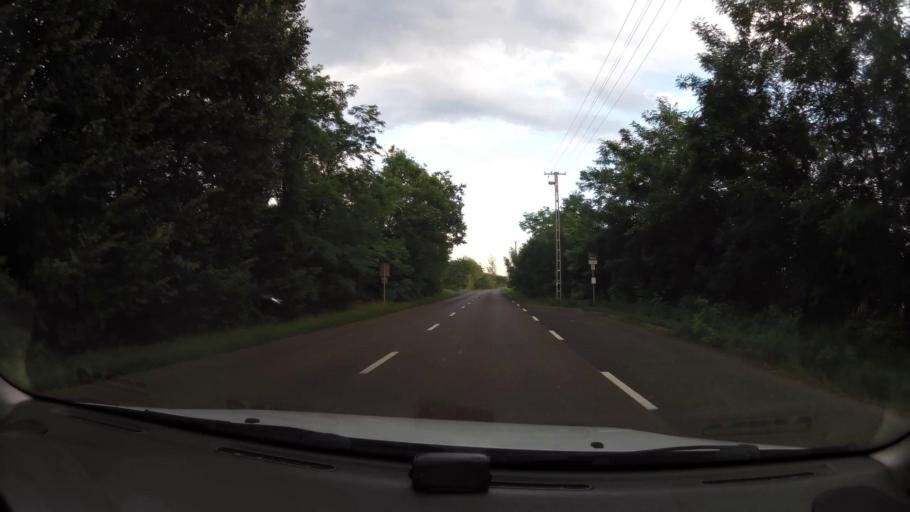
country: HU
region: Pest
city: Tapiobicske
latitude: 47.3754
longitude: 19.6704
